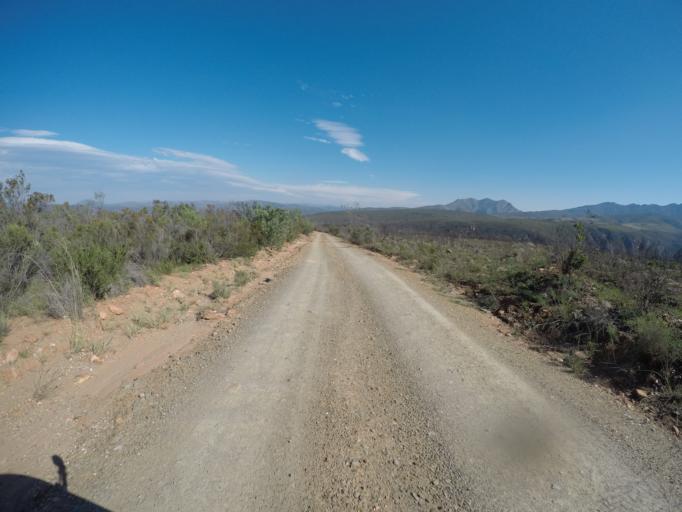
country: ZA
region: Eastern Cape
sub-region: Cacadu District Municipality
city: Kareedouw
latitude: -33.6364
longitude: 24.4544
